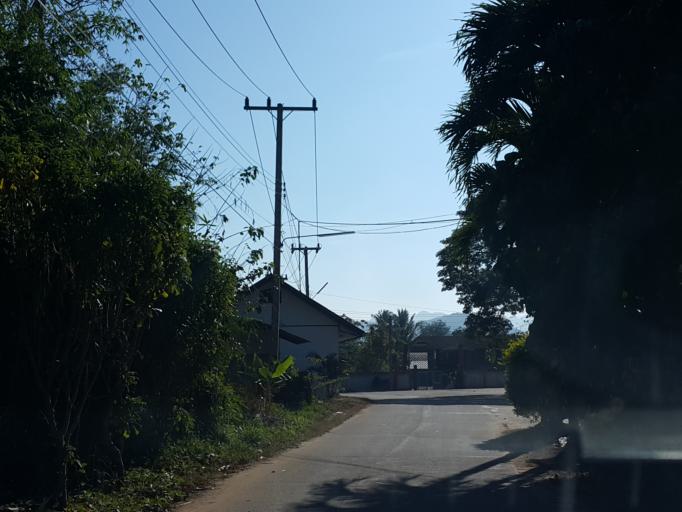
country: TH
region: Chiang Mai
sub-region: Amphoe Chiang Dao
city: Chiang Dao
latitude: 19.4672
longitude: 98.9572
